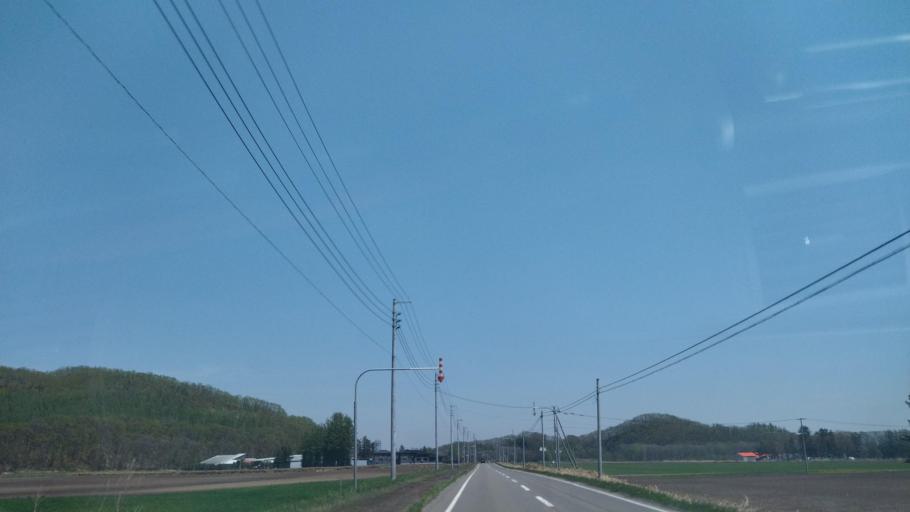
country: JP
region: Hokkaido
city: Obihiro
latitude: 42.8179
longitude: 142.9789
